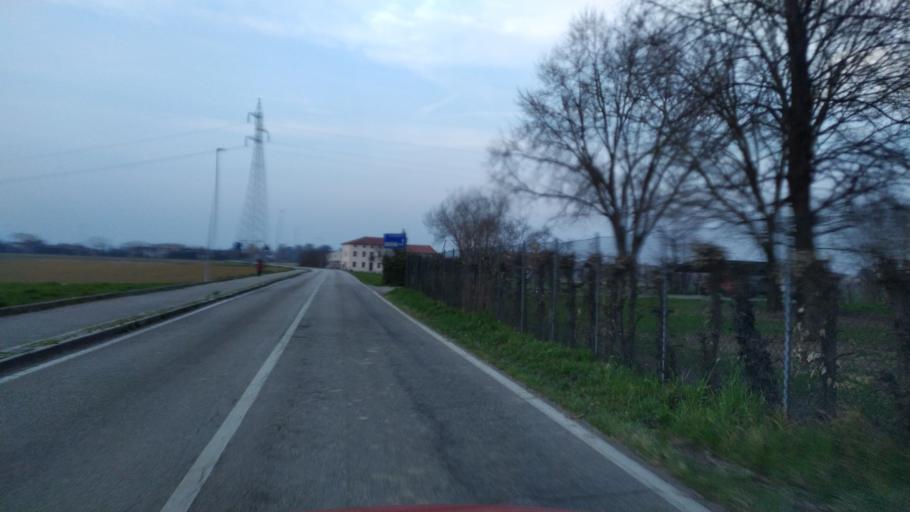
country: IT
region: Veneto
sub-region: Provincia di Vicenza
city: Vigardolo
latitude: 45.6006
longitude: 11.5822
